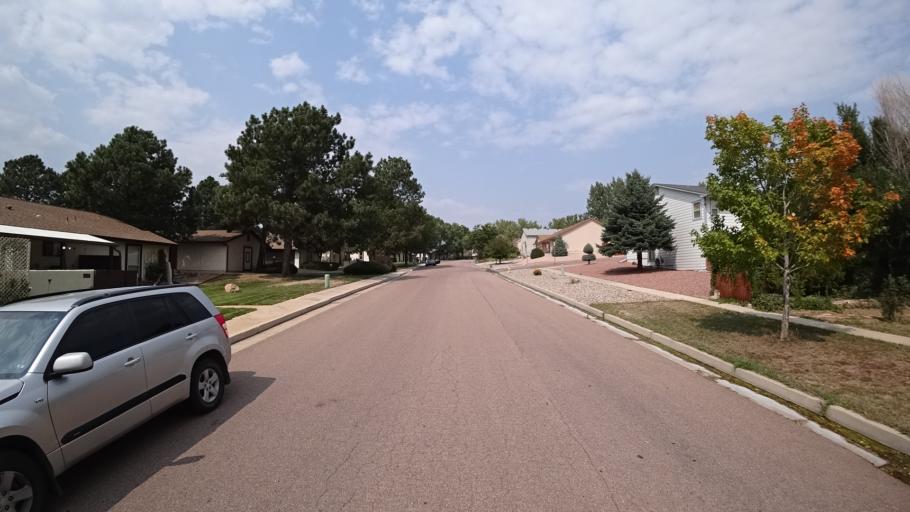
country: US
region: Colorado
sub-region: El Paso County
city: Stratmoor
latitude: 38.8232
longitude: -104.7661
